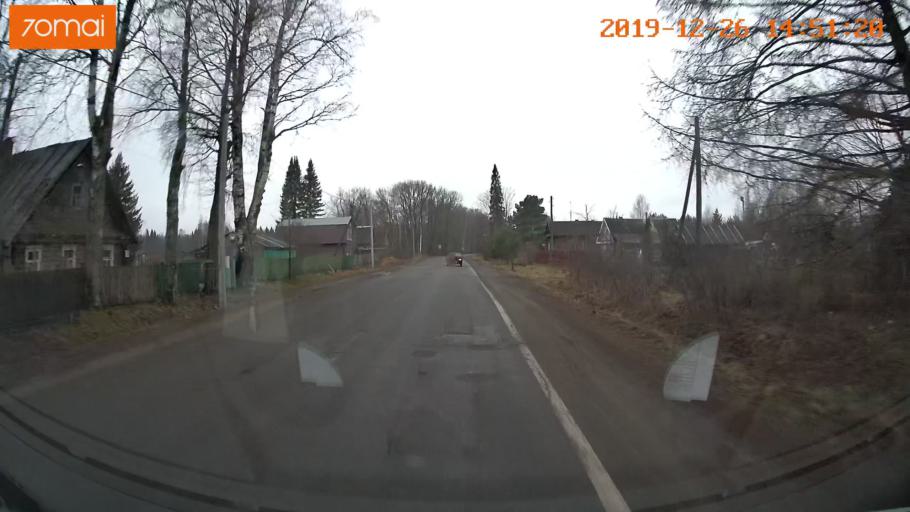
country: RU
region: Jaroslavl
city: Poshekhon'ye
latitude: 58.3262
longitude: 38.9122
